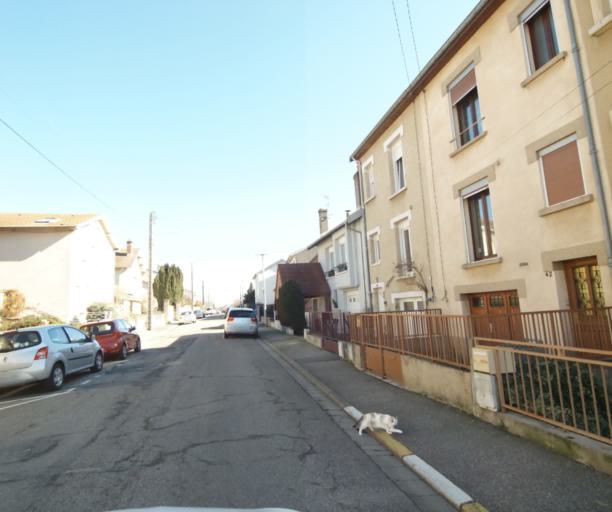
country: FR
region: Lorraine
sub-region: Departement de Meurthe-et-Moselle
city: Essey-les-Nancy
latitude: 48.7065
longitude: 6.2258
